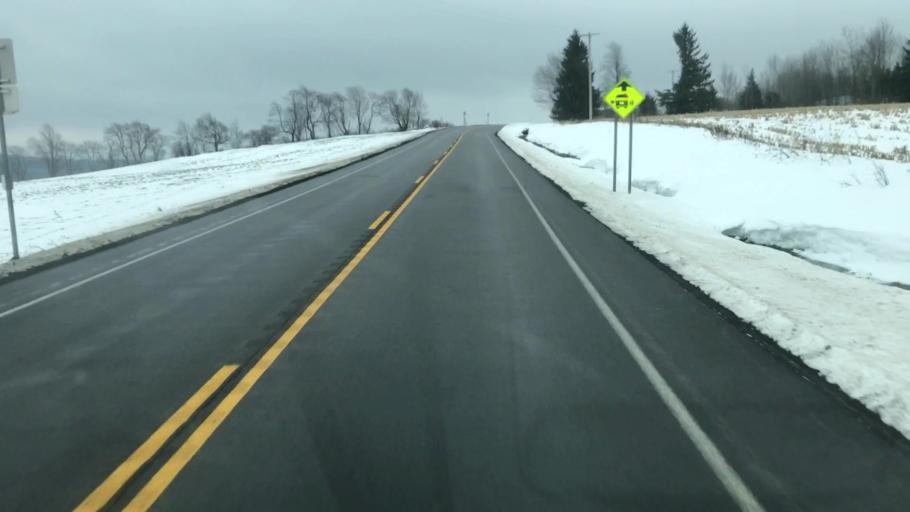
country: US
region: New York
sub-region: Cayuga County
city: Moravia
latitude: 42.7708
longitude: -76.3333
